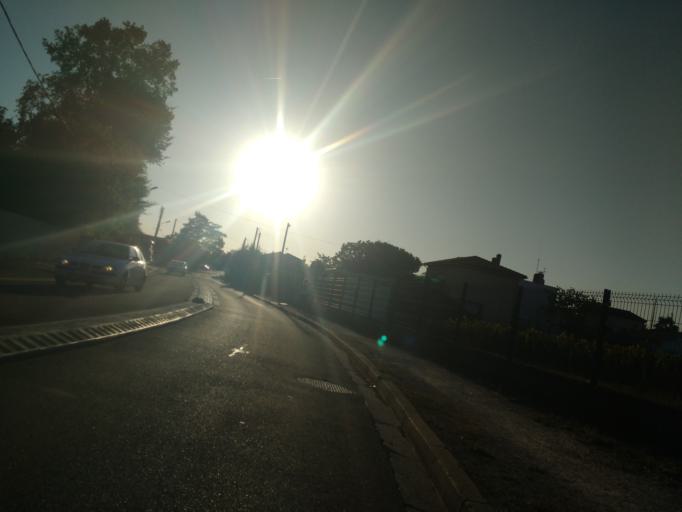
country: FR
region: Aquitaine
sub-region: Departement de la Gironde
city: Talence
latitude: 44.8084
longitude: -0.6149
